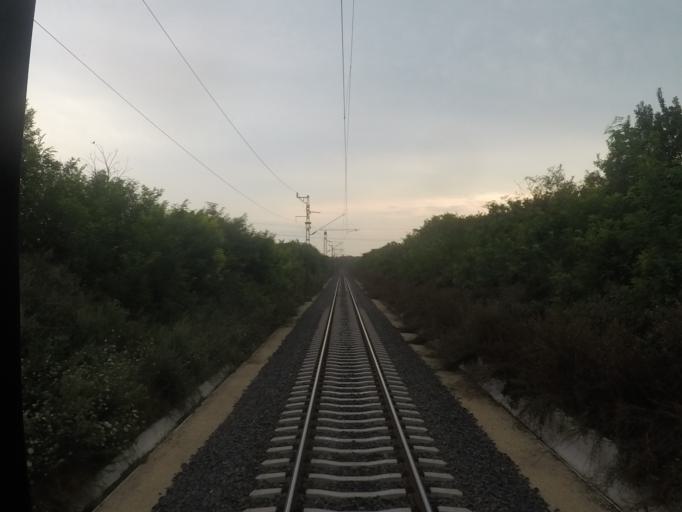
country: HU
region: Fejer
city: Lepseny
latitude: 46.9798
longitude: 18.2384
